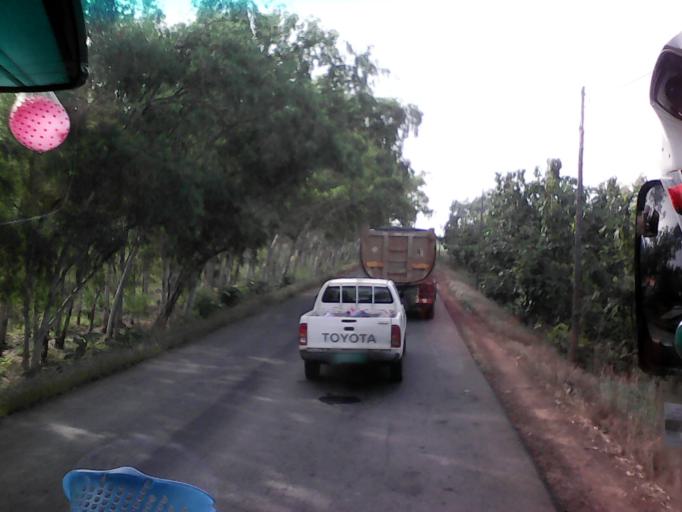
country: TG
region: Kara
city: Kara
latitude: 9.4806
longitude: 1.2098
